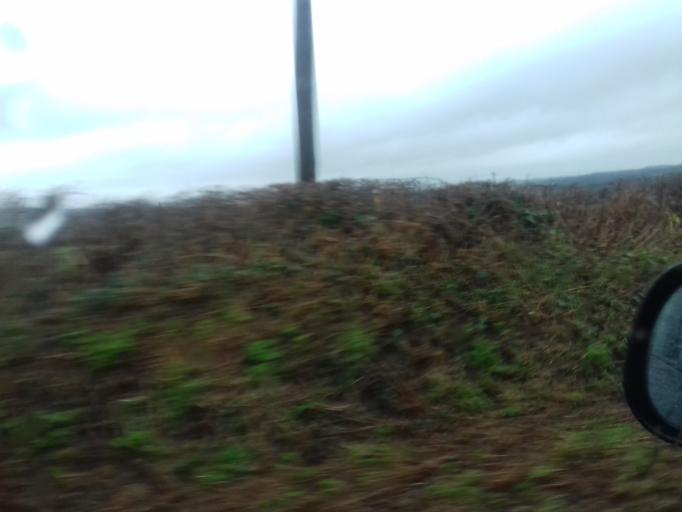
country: IE
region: Leinster
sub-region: Kilkenny
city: Graiguenamanagh
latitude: 52.5914
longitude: -7.0039
